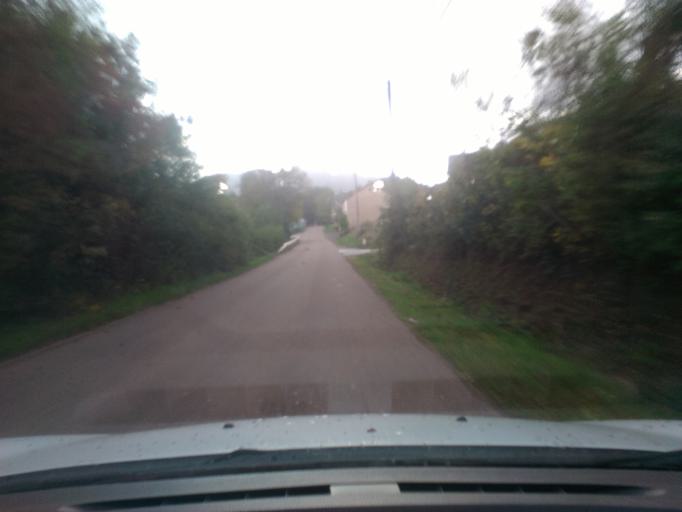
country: FR
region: Lorraine
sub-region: Departement des Vosges
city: Saint-Die-des-Vosges
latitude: 48.3084
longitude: 6.9578
